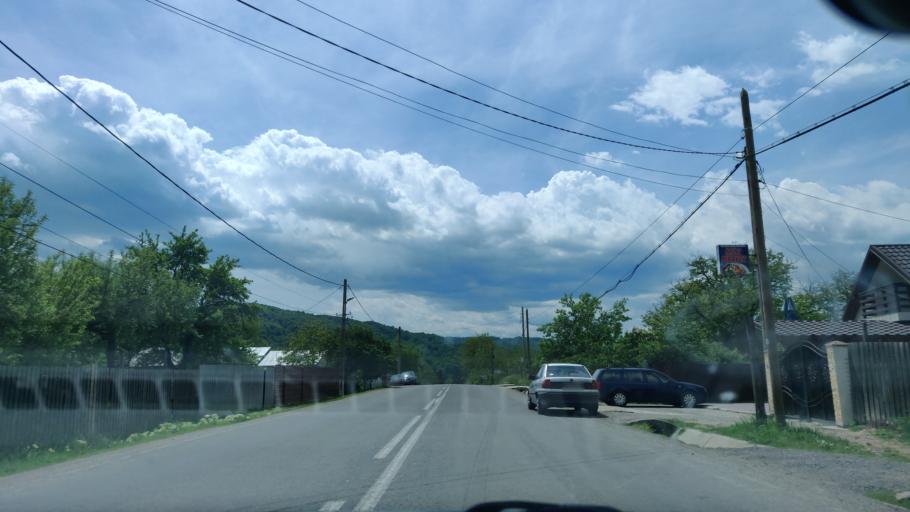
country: RO
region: Vrancea
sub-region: Comuna Vidra
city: Vidra
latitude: 45.9011
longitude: 26.8885
